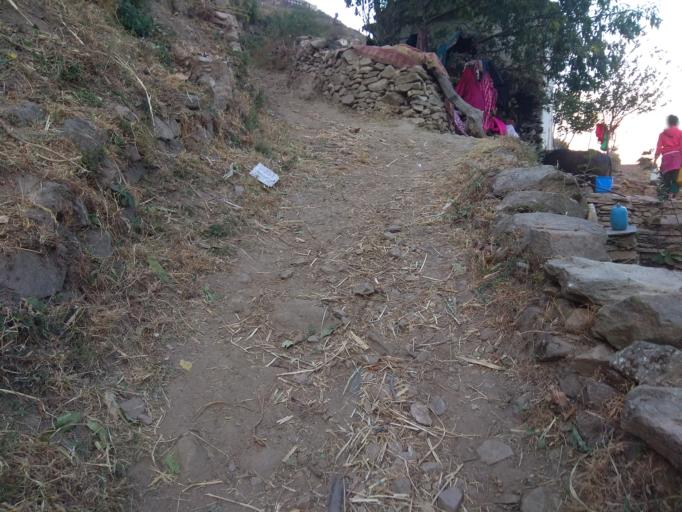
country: NP
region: Mid Western
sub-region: Karnali Zone
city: Jumla
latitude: 29.3241
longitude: 81.7229
